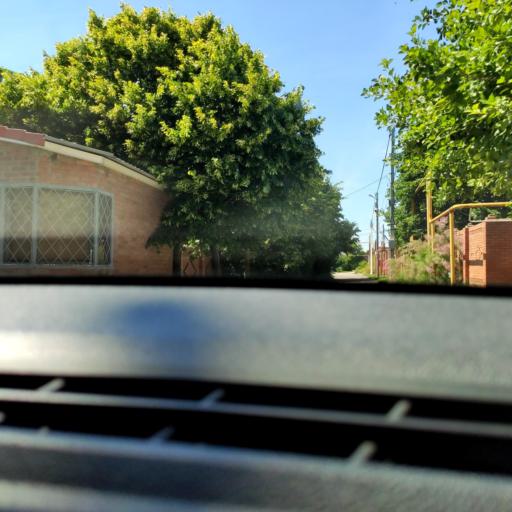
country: RU
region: Samara
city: Podstepki
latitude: 53.5072
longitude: 49.2400
